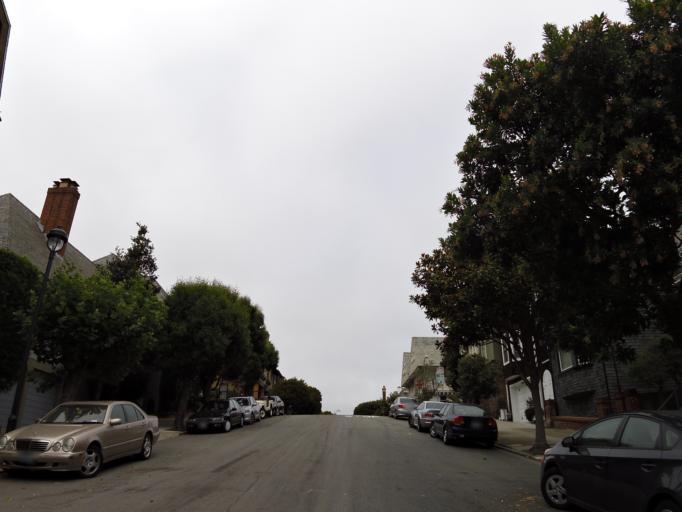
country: US
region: California
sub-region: San Francisco County
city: San Francisco
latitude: 37.7876
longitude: -122.4553
